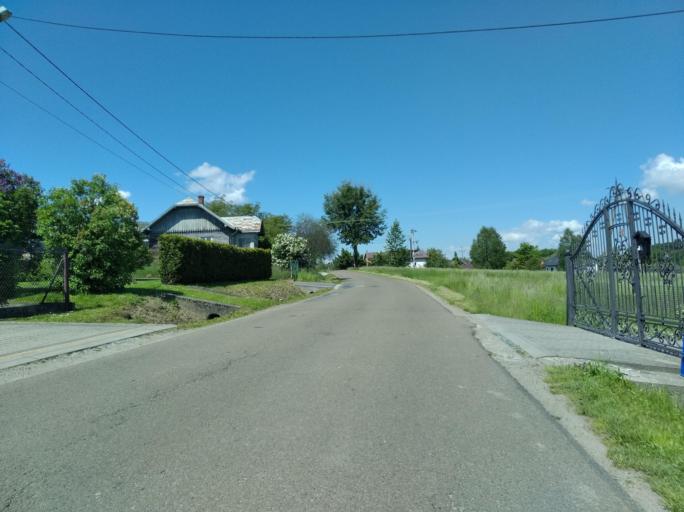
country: PL
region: Subcarpathian Voivodeship
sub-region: Powiat jasielski
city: Tarnowiec
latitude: 49.7118
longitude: 21.6075
